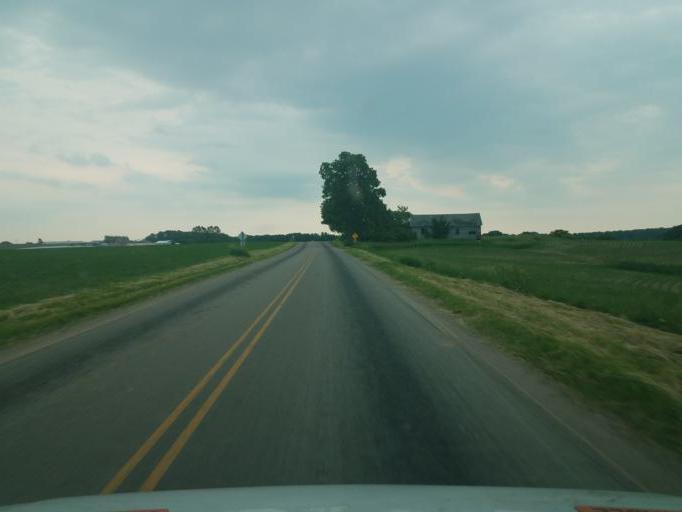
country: US
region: Wisconsin
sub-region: Vernon County
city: Hillsboro
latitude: 43.6176
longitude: -90.4489
